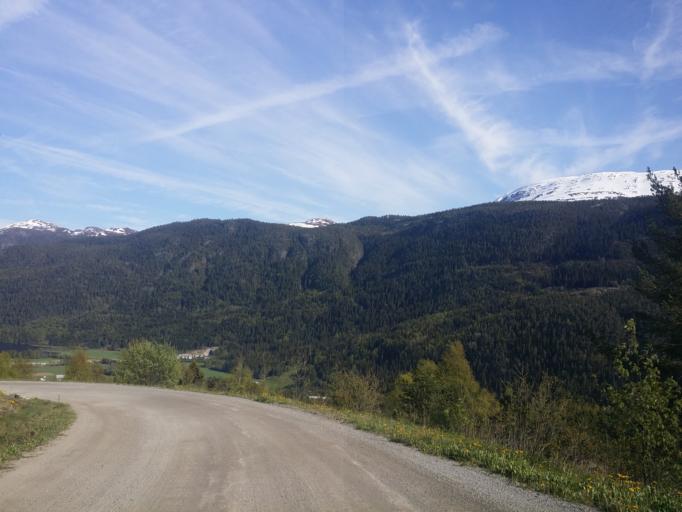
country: NO
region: Telemark
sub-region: Seljord
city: Seljord
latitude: 59.6073
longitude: 8.6831
